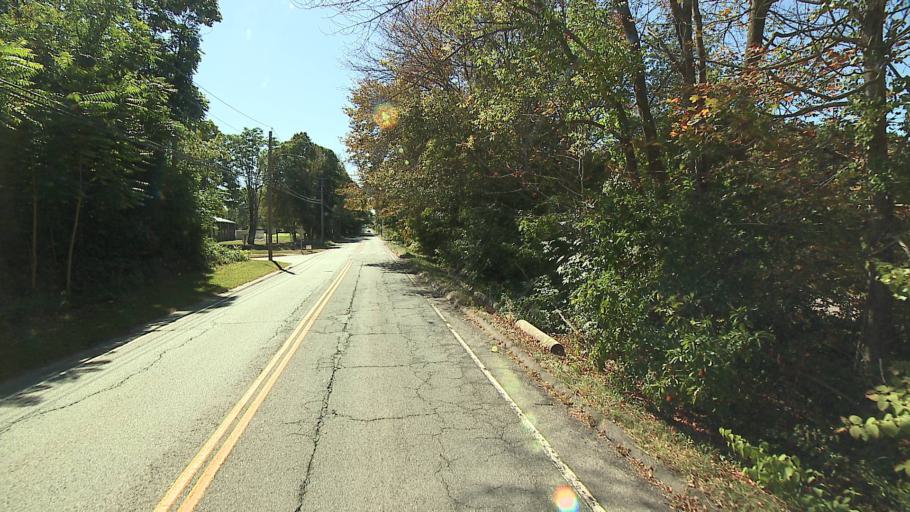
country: US
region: Connecticut
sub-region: New Haven County
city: Milford
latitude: 41.2532
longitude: -73.0507
